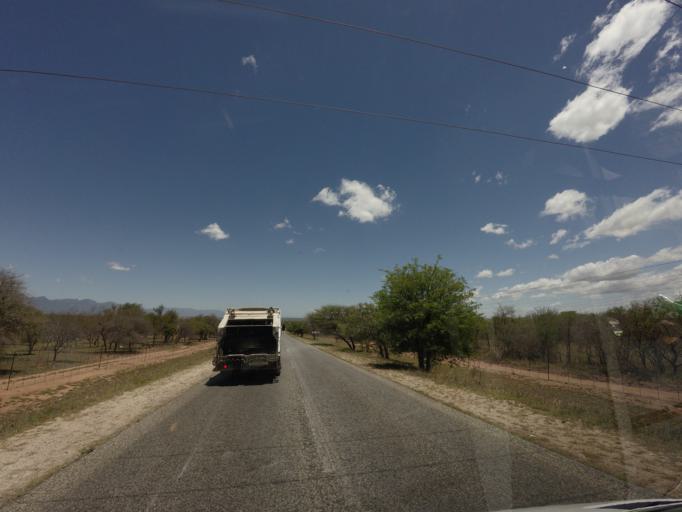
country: ZA
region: Limpopo
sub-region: Mopani District Municipality
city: Hoedspruit
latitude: -24.3964
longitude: 30.7615
